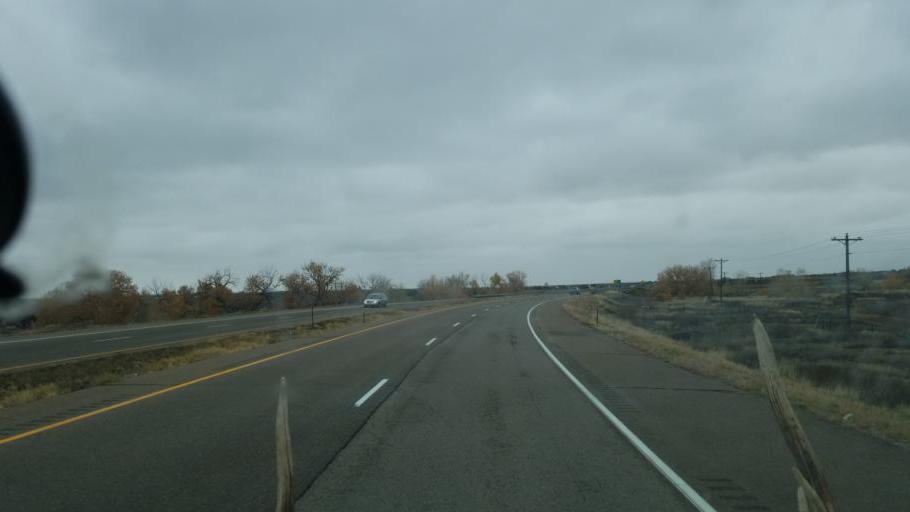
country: US
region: Colorado
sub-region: Pueblo County
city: Pueblo
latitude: 38.2668
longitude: -104.3749
